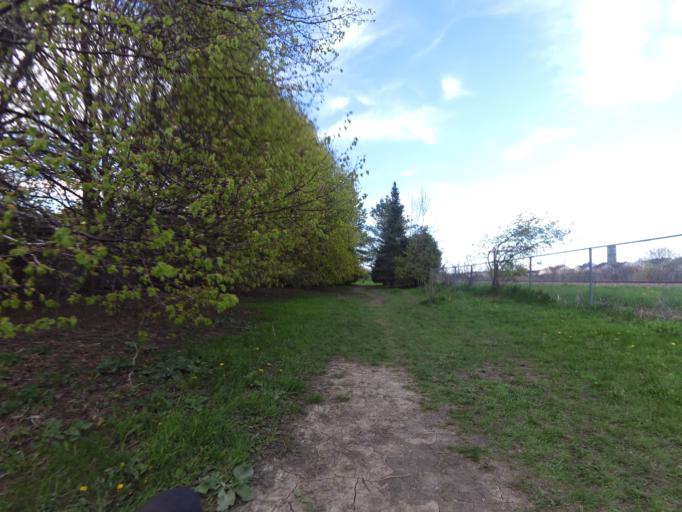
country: CA
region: Ontario
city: Bells Corners
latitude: 45.2901
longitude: -75.7441
